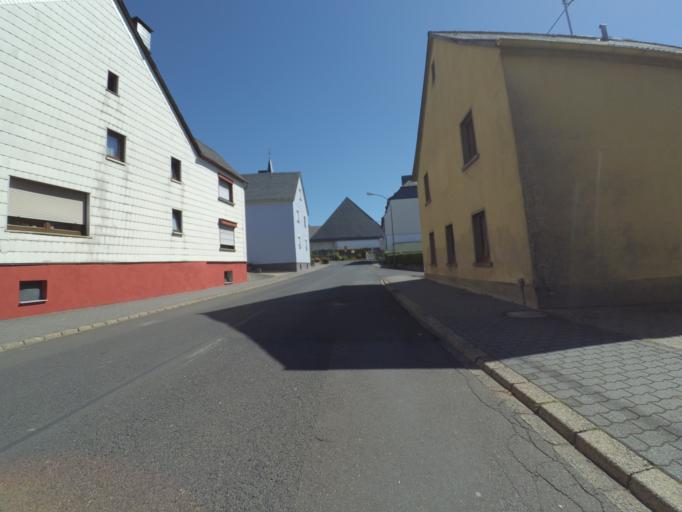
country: DE
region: Rheinland-Pfalz
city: Beuren
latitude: 50.0946
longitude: 7.0787
